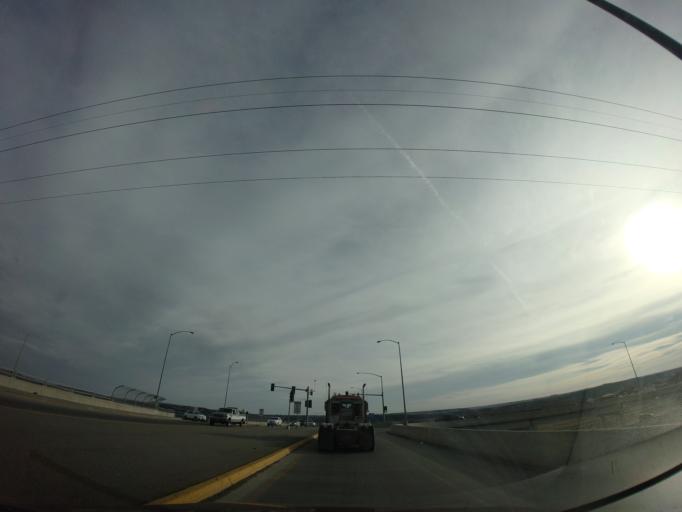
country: US
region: Montana
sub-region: Yellowstone County
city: Billings
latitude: 45.7325
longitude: -108.6044
